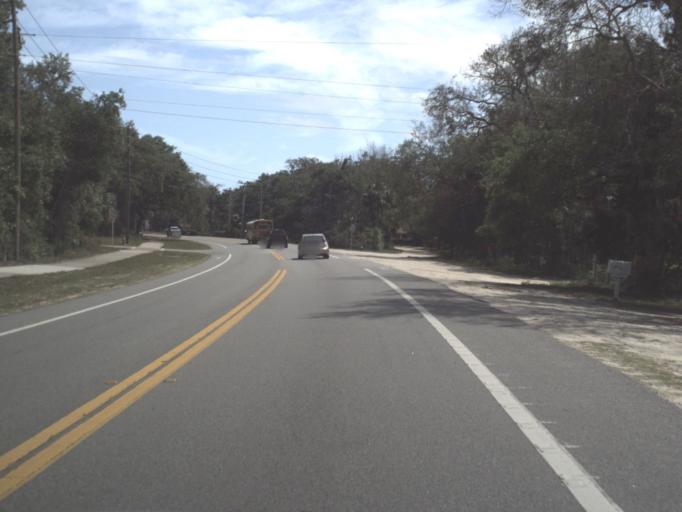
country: US
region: Florida
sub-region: Flagler County
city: Palm Coast
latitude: 29.5922
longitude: -81.1938
